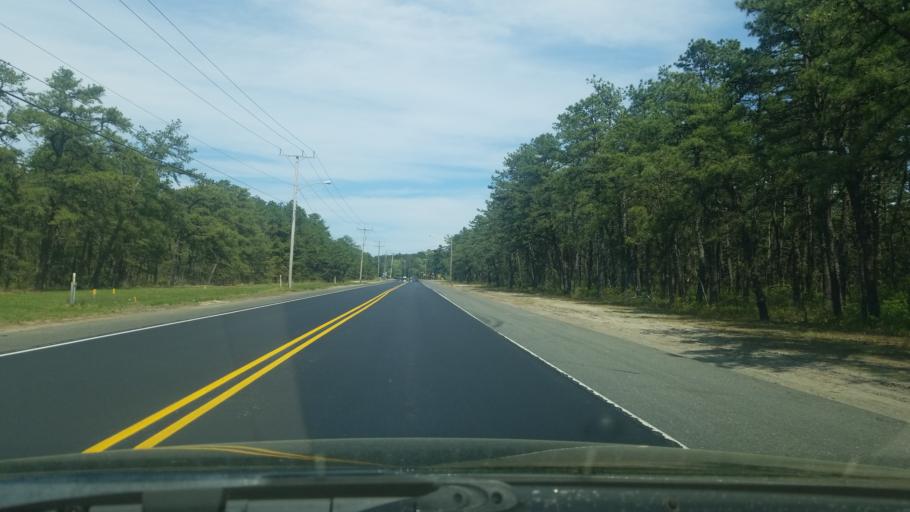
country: US
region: New Jersey
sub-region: Ocean County
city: Lakehurst
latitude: 40.0062
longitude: -74.3371
